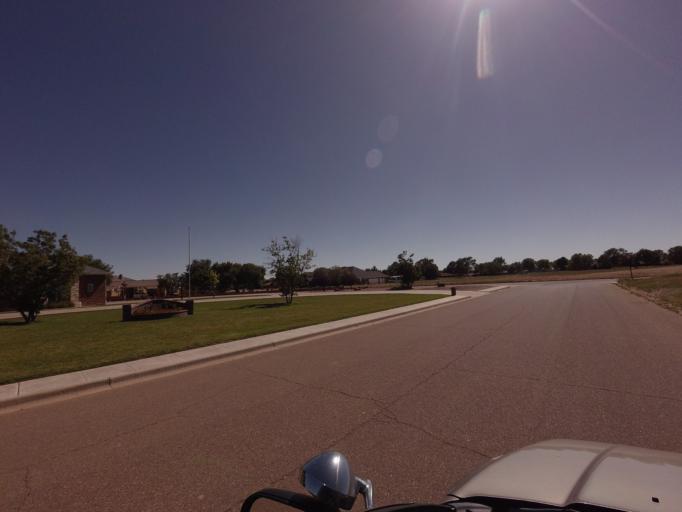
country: US
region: New Mexico
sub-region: Curry County
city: Clovis
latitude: 34.4468
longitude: -103.1899
